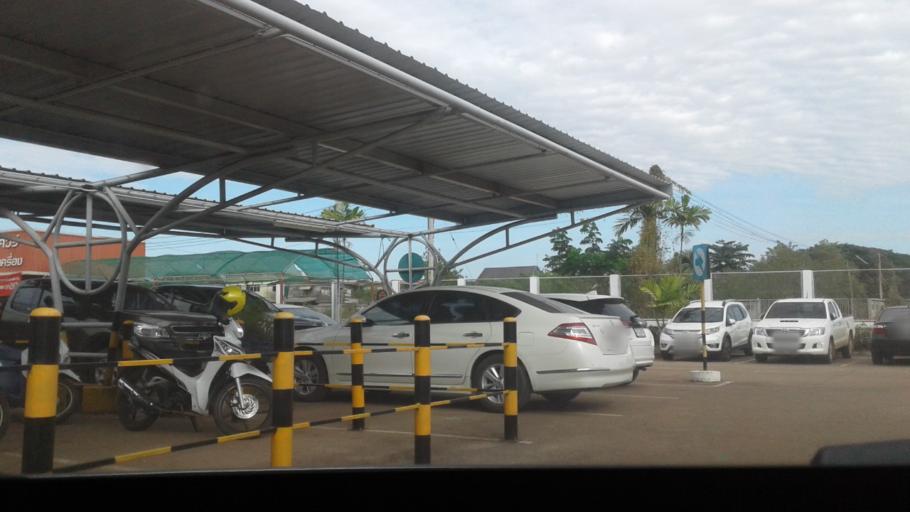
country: TH
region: Changwat Udon Thani
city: Udon Thani
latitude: 17.4308
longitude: 102.7878
